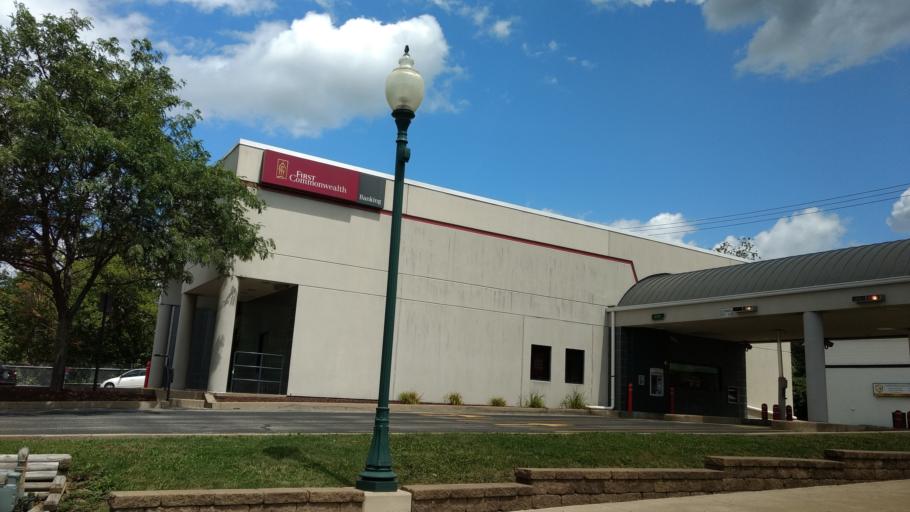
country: US
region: Pennsylvania
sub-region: Westmoreland County
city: Murrysville
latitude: 40.4284
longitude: -79.6983
